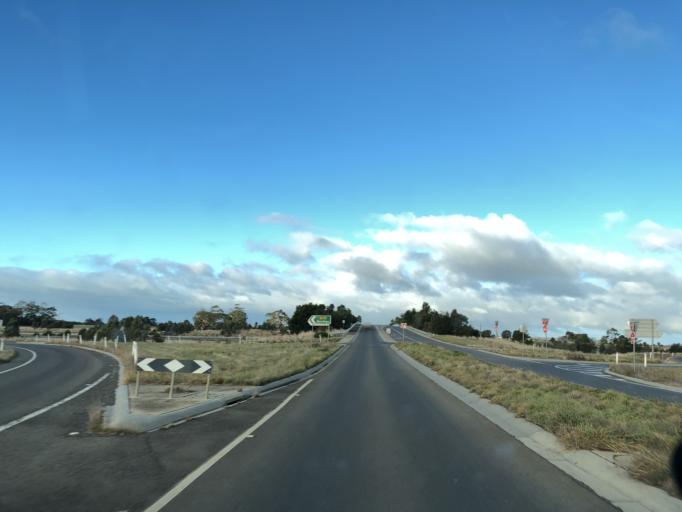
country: AU
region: Victoria
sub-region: Mount Alexander
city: Castlemaine
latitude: -37.1915
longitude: 144.4013
